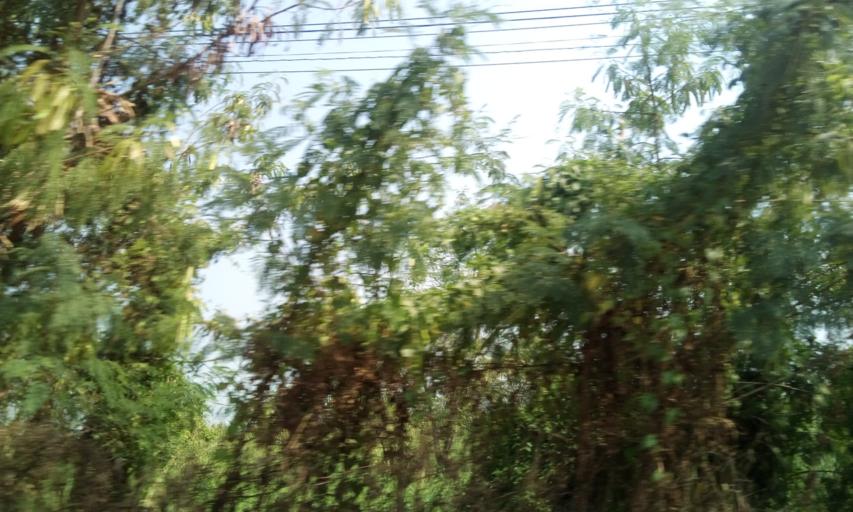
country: TH
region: Pathum Thani
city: Ban Rangsit
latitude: 14.0128
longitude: 100.7581
